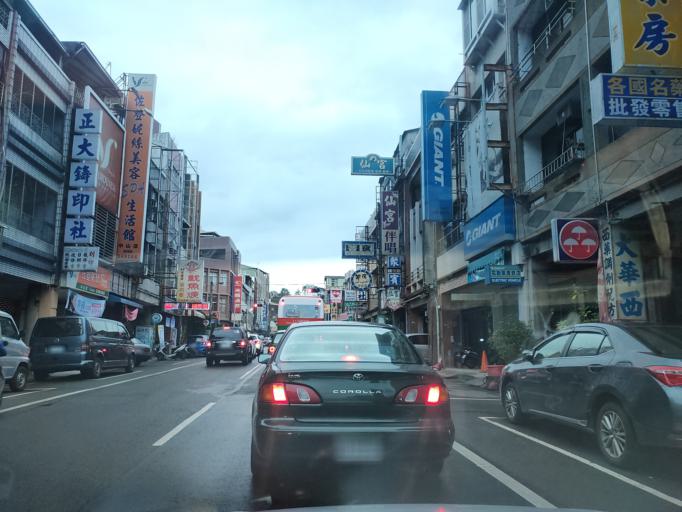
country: TW
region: Taiwan
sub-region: Miaoli
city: Miaoli
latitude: 24.5556
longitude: 120.8170
